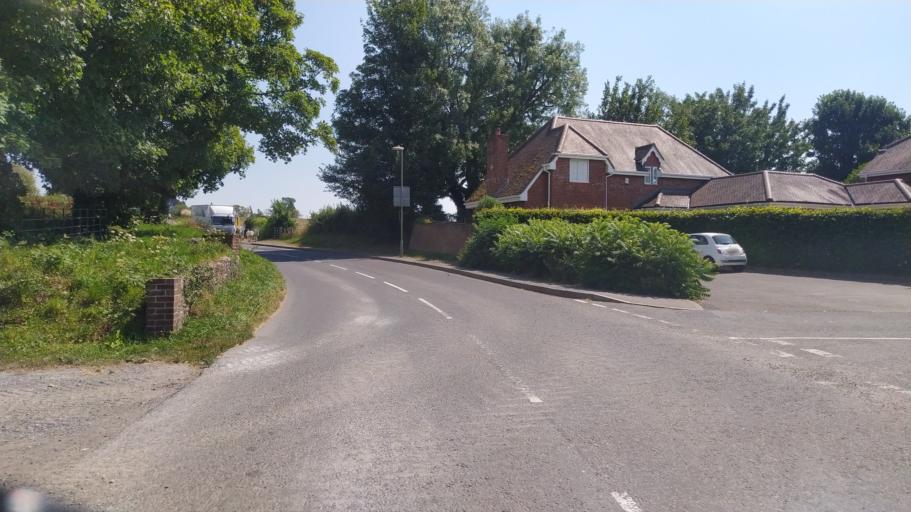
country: GB
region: England
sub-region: Hampshire
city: Cowplain
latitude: 50.9464
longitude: -1.0066
